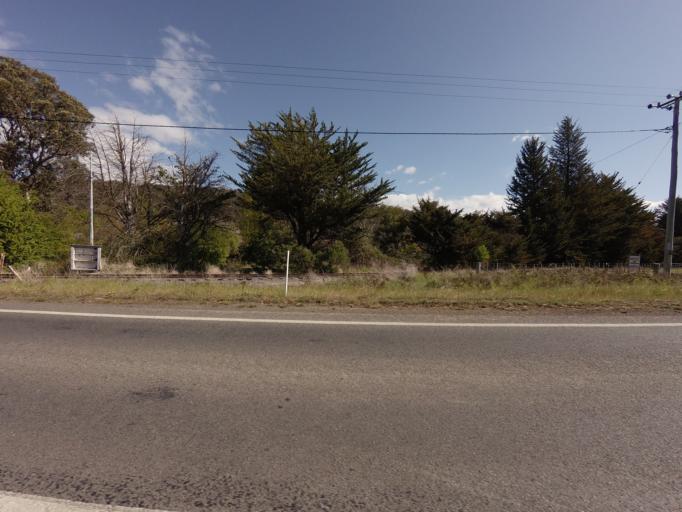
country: AU
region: Tasmania
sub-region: Derwent Valley
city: New Norfolk
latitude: -42.7775
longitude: 147.0392
